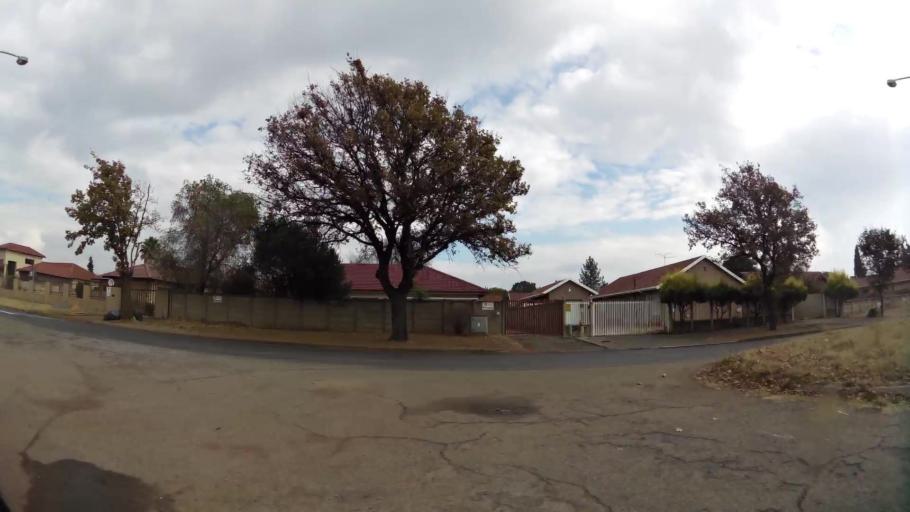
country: ZA
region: Gauteng
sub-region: Sedibeng District Municipality
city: Vanderbijlpark
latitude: -26.7224
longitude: 27.8629
